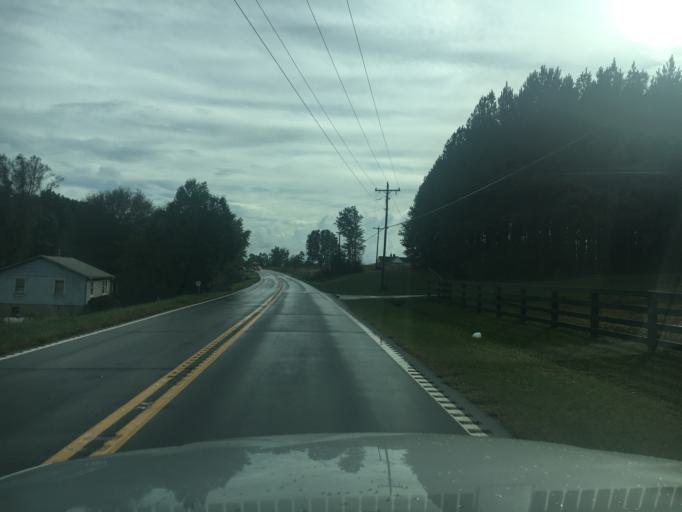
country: US
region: North Carolina
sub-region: Rutherford County
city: Spindale
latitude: 35.4503
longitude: -81.8891
